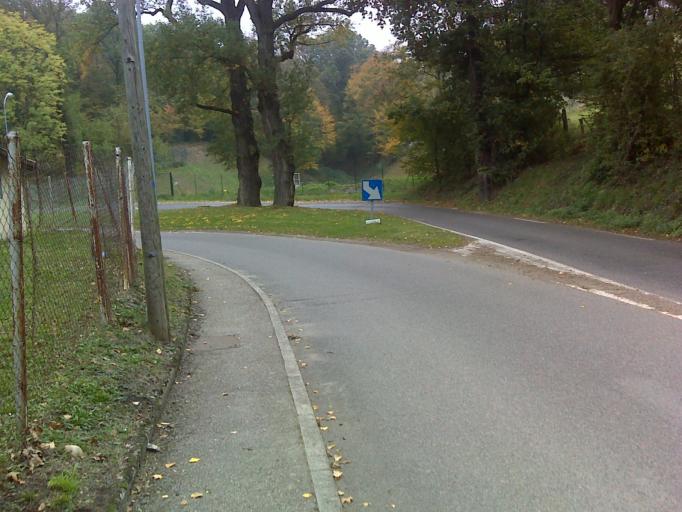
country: FR
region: Rhone-Alpes
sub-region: Departement de la Loire
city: Saint-Jean-Bonnefonds
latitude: 45.4658
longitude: 4.4423
